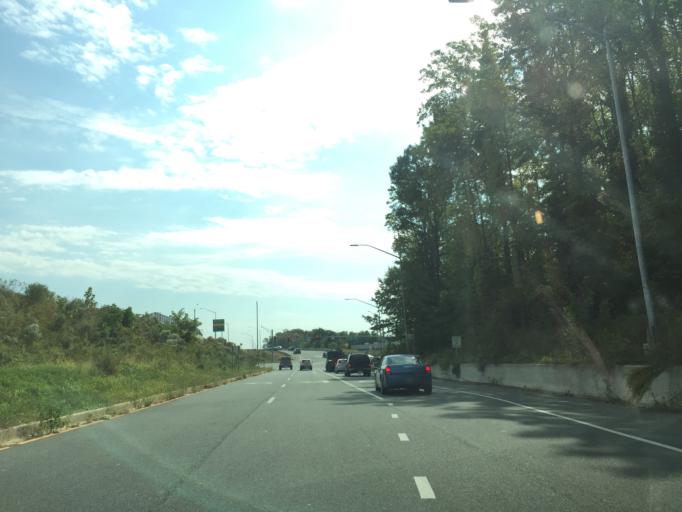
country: US
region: Maryland
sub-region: Harford County
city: Bel Air South
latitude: 39.4657
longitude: -76.3147
